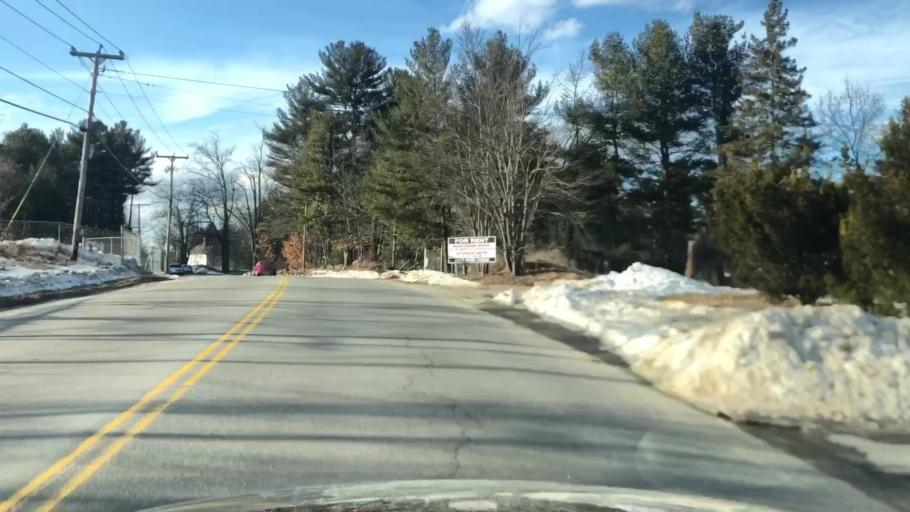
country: US
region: New Hampshire
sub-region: Hillsborough County
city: Milford
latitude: 42.8433
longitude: -71.6630
